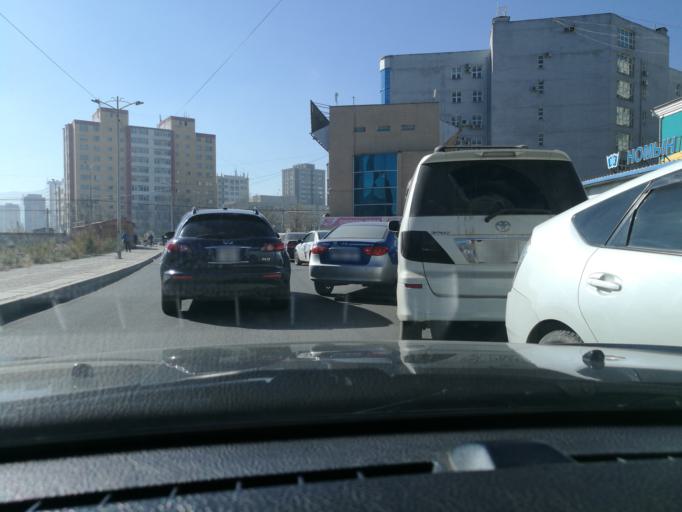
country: MN
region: Ulaanbaatar
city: Ulaanbaatar
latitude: 47.9192
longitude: 106.9296
